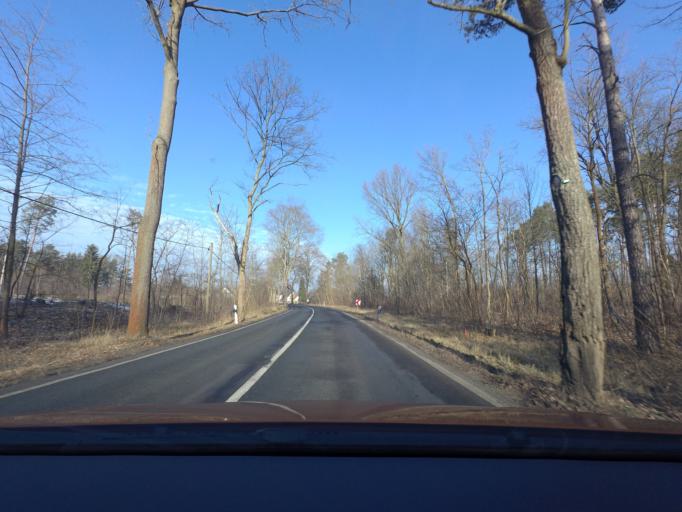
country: DE
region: Brandenburg
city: Wandlitz
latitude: 52.7491
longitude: 13.3740
